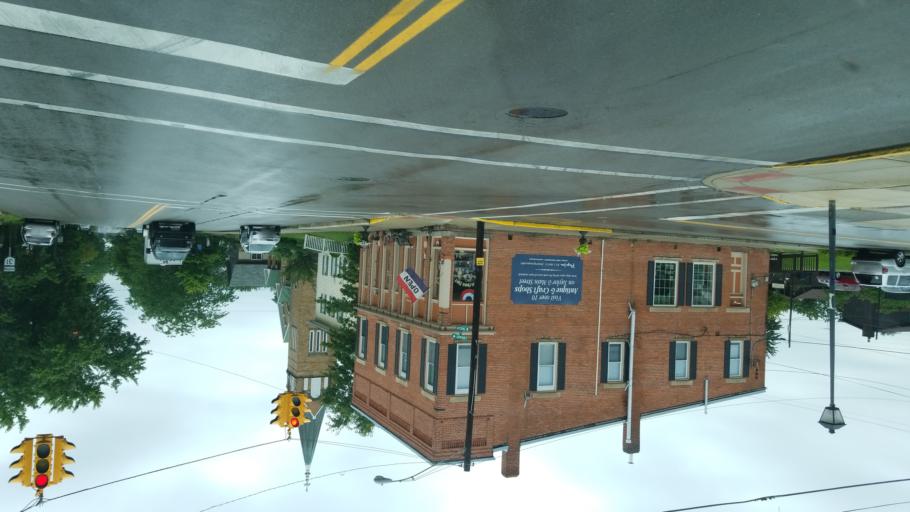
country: US
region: Ohio
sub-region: Hardin County
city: Kenton
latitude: 40.5342
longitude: -83.5209
